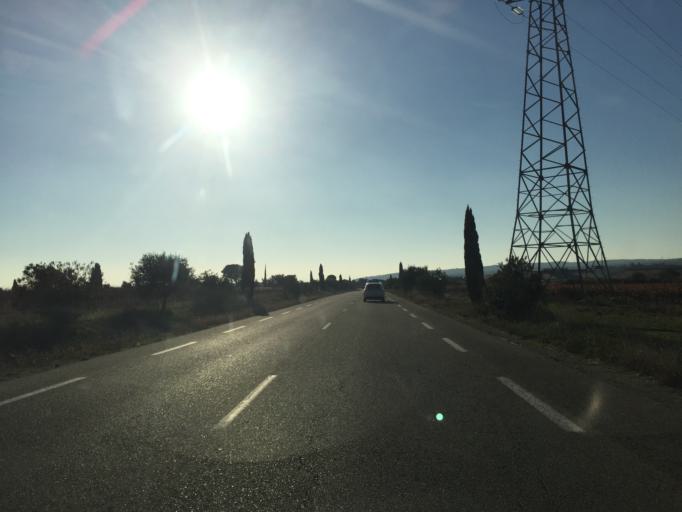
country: FR
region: Provence-Alpes-Cote d'Azur
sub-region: Departement du Vaucluse
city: Sainte-Cecile-les-Vignes
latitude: 44.2169
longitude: 4.8736
